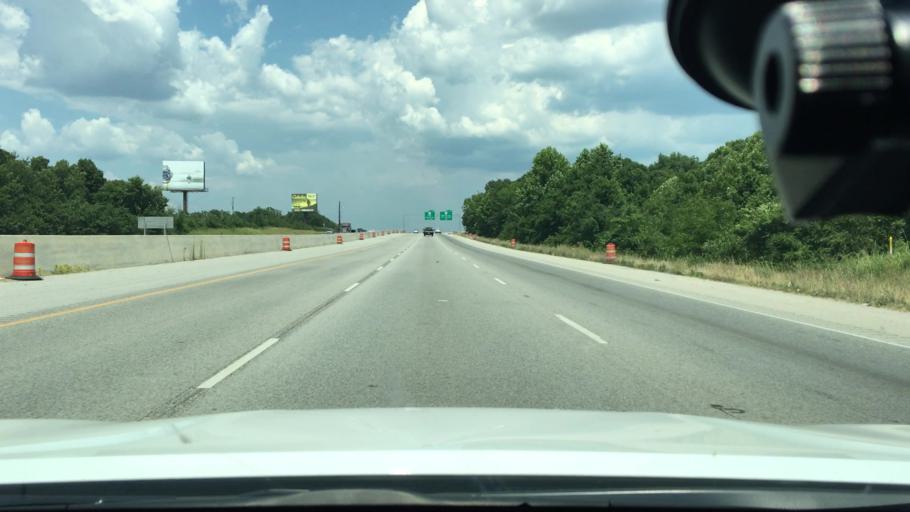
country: US
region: Arkansas
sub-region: Benton County
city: Bethel Heights
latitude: 36.2322
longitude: -94.1730
